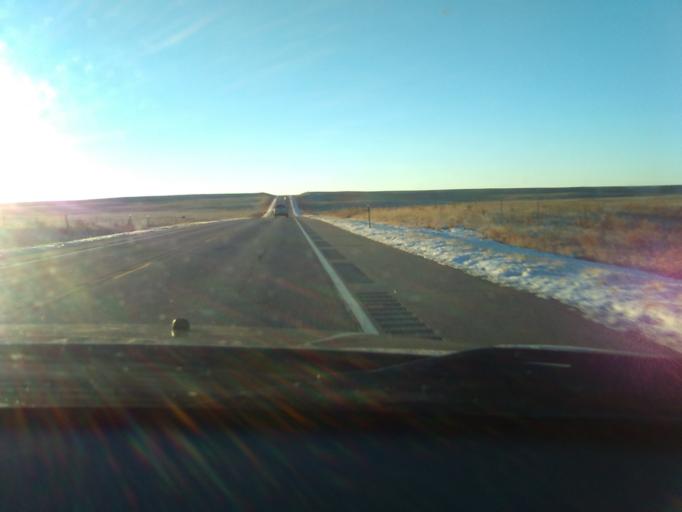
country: US
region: Colorado
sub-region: Logan County
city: Sterling
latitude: 40.6788
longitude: -102.9609
